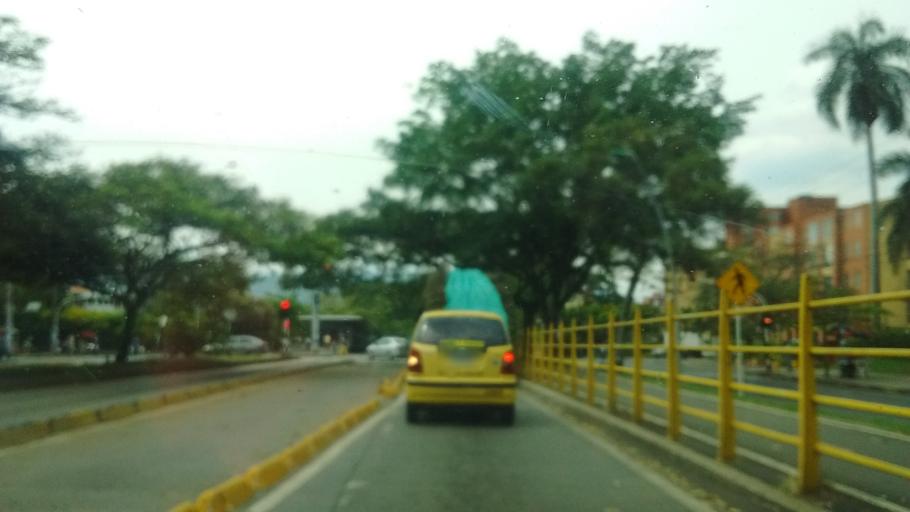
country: CO
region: Valle del Cauca
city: Cali
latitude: 3.3761
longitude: -76.5424
